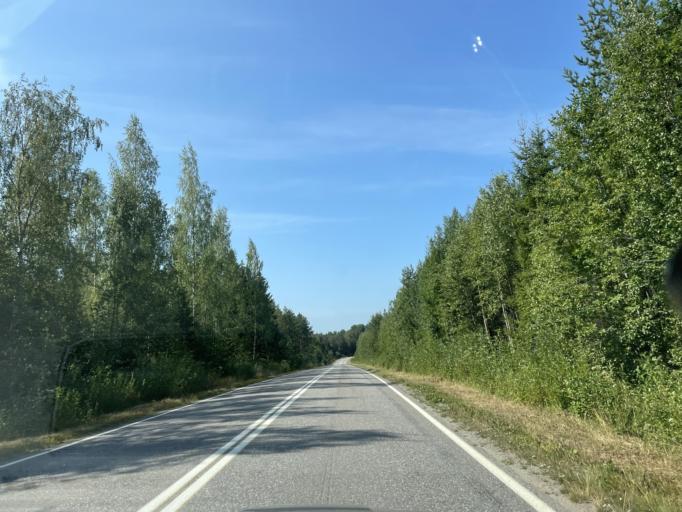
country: FI
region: Central Finland
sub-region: Saarijaervi-Viitasaari
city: Pihtipudas
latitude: 63.3647
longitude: 25.6623
